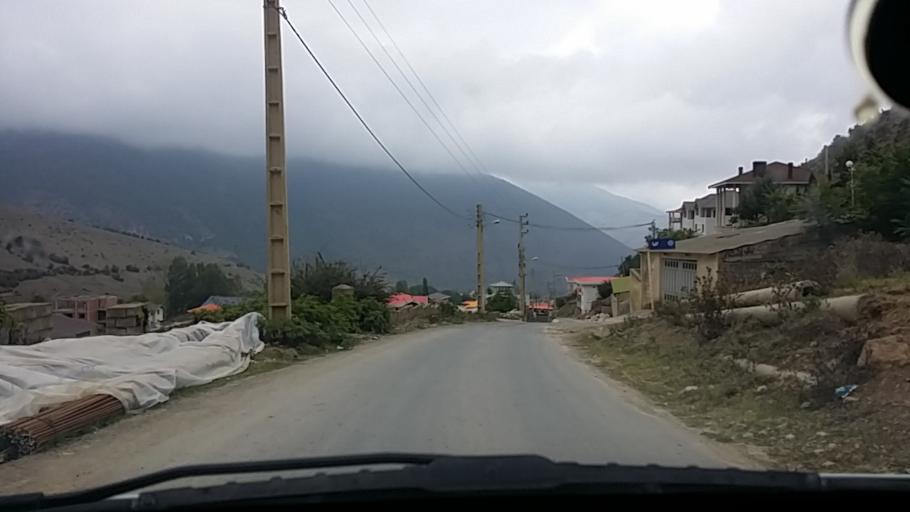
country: IR
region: Mazandaran
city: `Abbasabad
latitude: 36.4746
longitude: 51.1401
